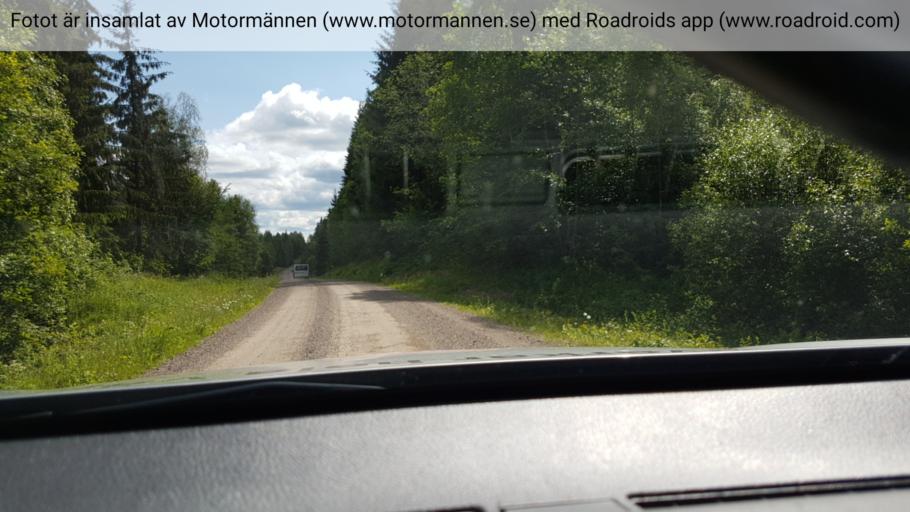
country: SE
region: Vaermland
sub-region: Hagfors Kommun
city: Ekshaerad
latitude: 60.3494
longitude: 13.3190
